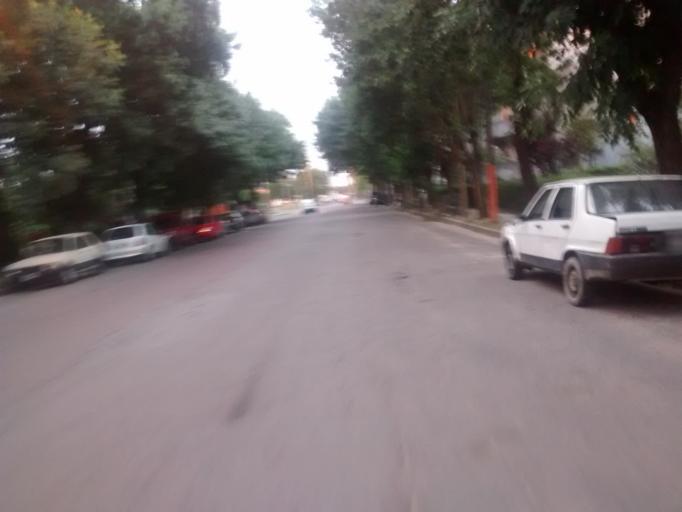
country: AR
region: Buenos Aires
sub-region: Partido de La Plata
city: La Plata
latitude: -34.9414
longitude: -57.9242
